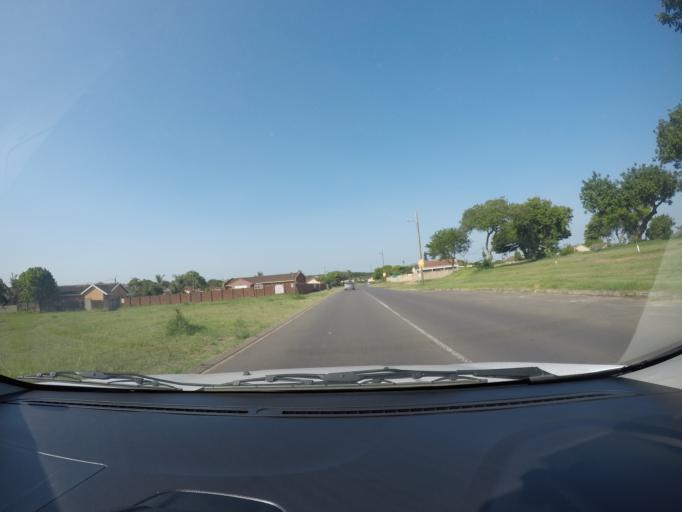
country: ZA
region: KwaZulu-Natal
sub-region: uThungulu District Municipality
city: Richards Bay
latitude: -28.7206
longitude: 32.0418
